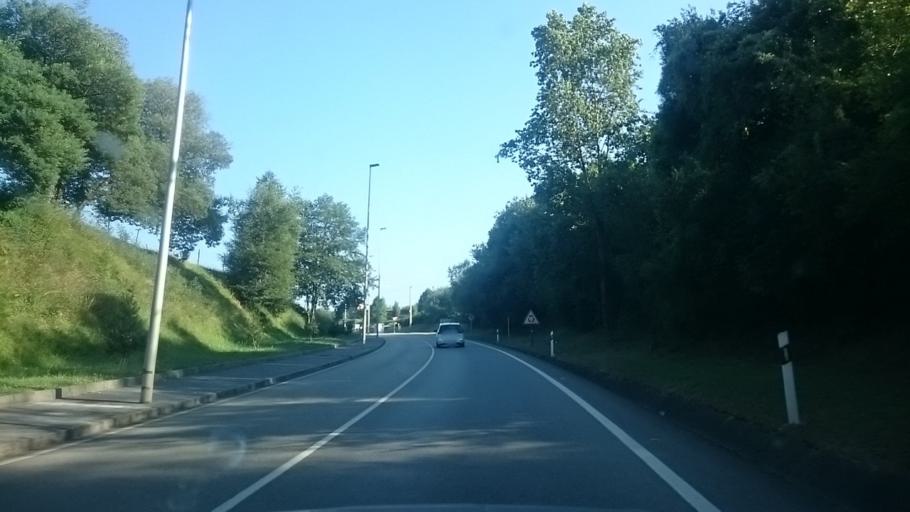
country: ES
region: Asturias
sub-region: Province of Asturias
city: Oviedo
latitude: 43.3264
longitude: -5.8770
